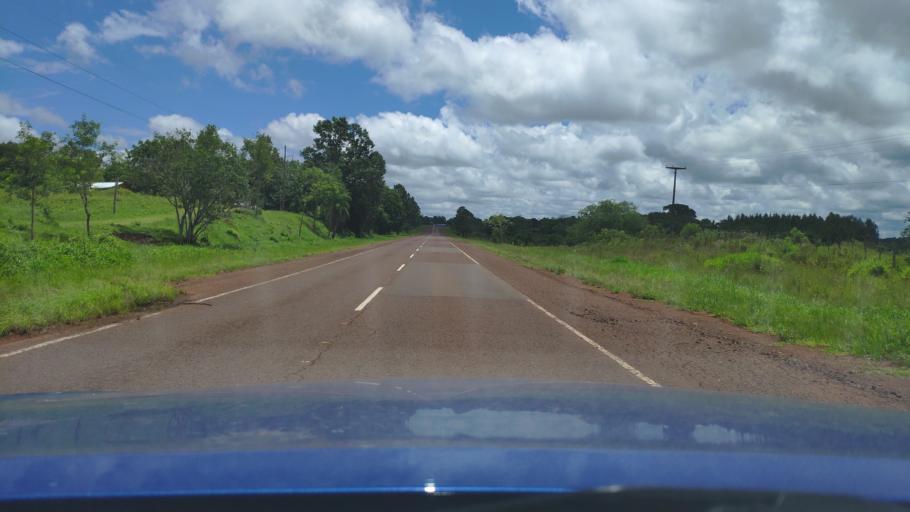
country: AR
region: Misiones
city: Dos Arroyos
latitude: -27.7469
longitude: -55.2586
